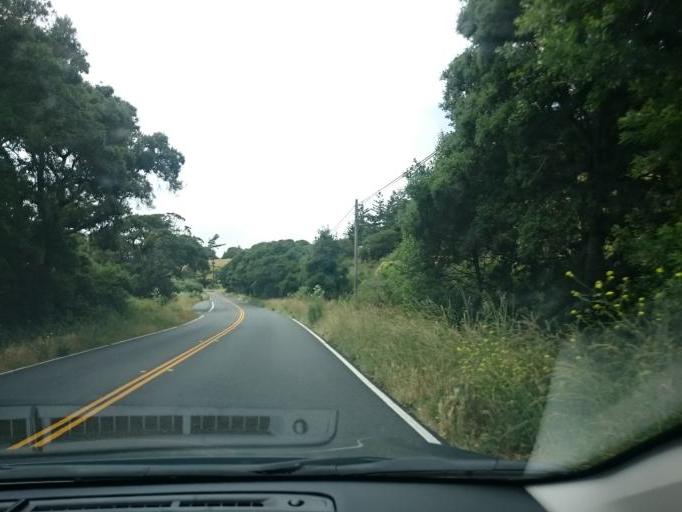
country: US
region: California
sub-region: Marin County
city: Lagunitas-Forest Knolls
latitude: 37.9769
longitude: -122.7334
